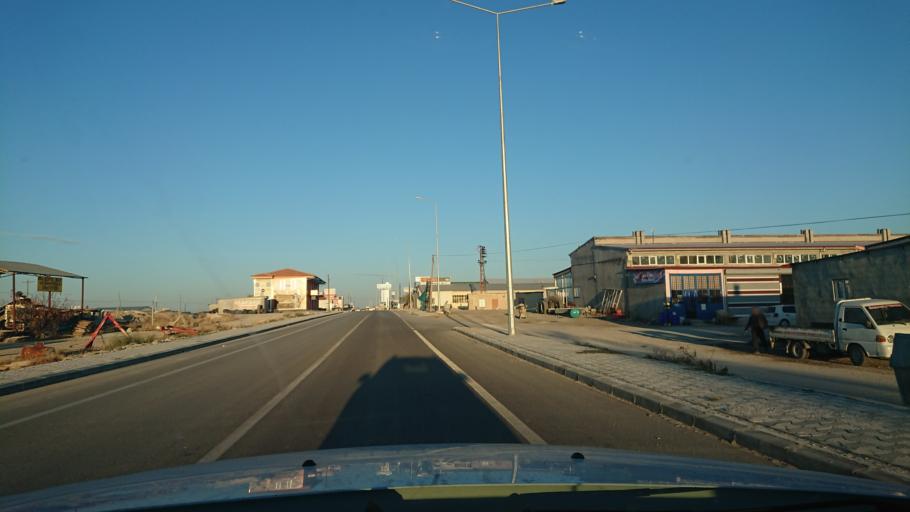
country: TR
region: Aksaray
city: Eskil
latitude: 38.3934
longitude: 33.3940
